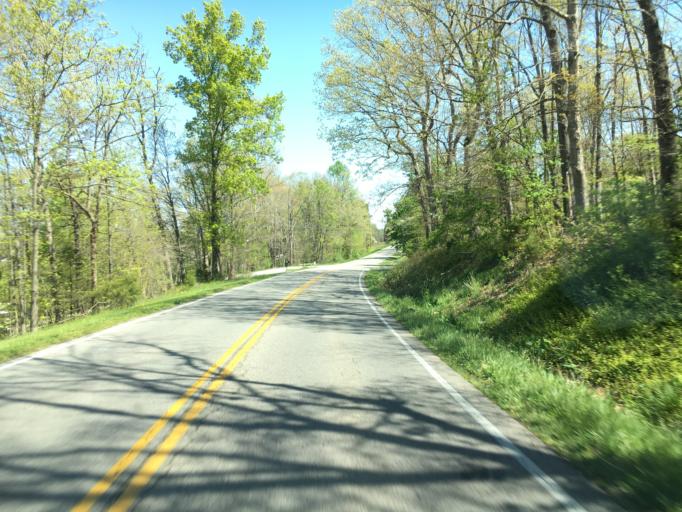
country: US
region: Virginia
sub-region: Augusta County
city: Crimora
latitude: 38.1659
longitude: -78.8506
